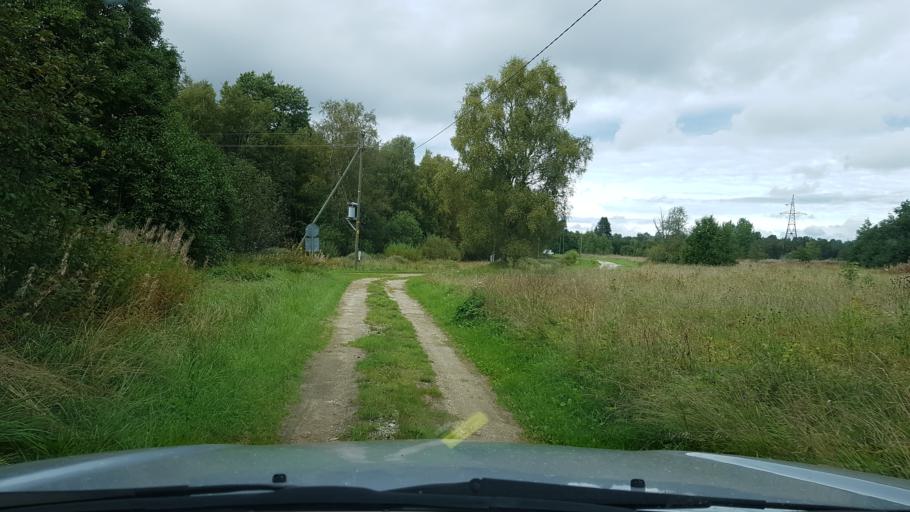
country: EE
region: Harju
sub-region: Raasiku vald
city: Arukula
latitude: 59.3595
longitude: 25.0036
